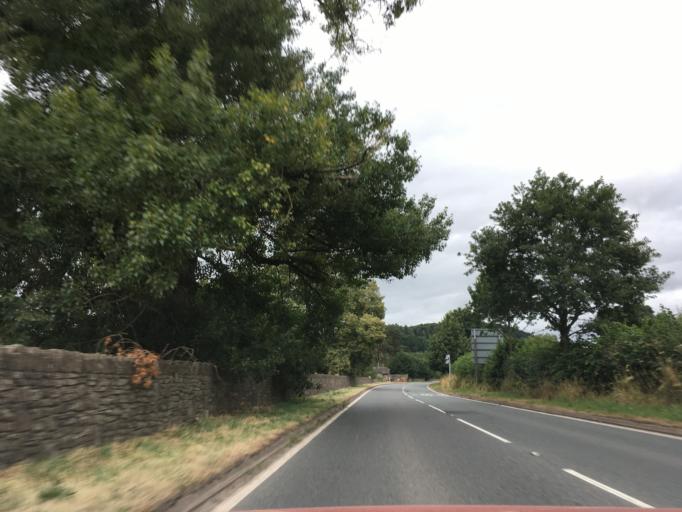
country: GB
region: Wales
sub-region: Blaenau Gwent
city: Brynmawr
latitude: 51.8720
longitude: -3.1686
